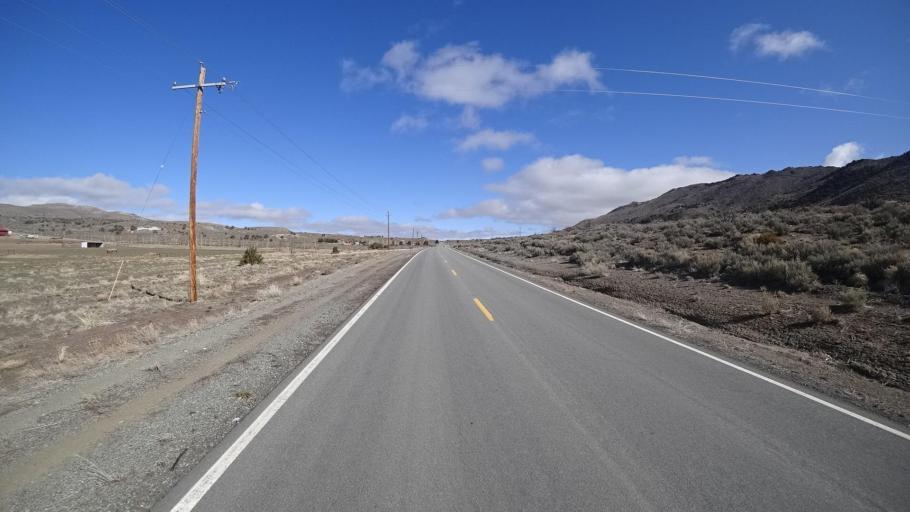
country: US
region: Nevada
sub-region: Washoe County
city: Cold Springs
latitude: 39.7493
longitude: -119.8861
